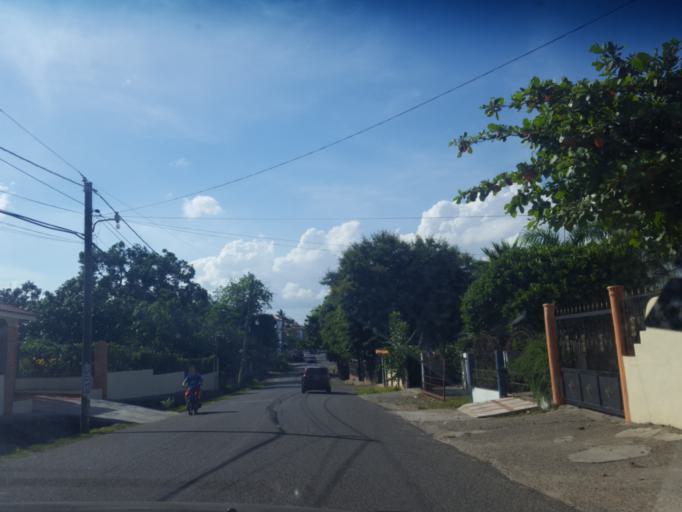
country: DO
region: La Vega
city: Rio Verde Arriba
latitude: 19.3560
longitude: -70.6043
